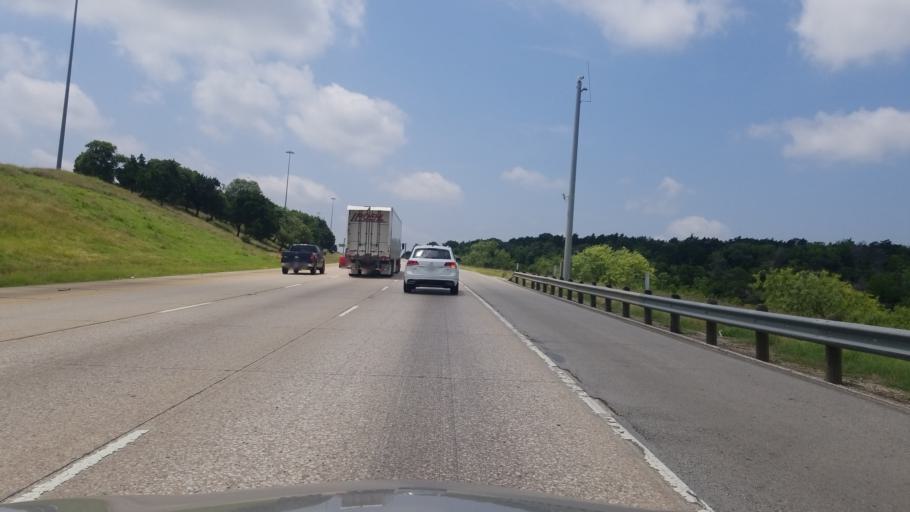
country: US
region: Texas
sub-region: Dallas County
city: Duncanville
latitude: 32.6817
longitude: -96.9454
